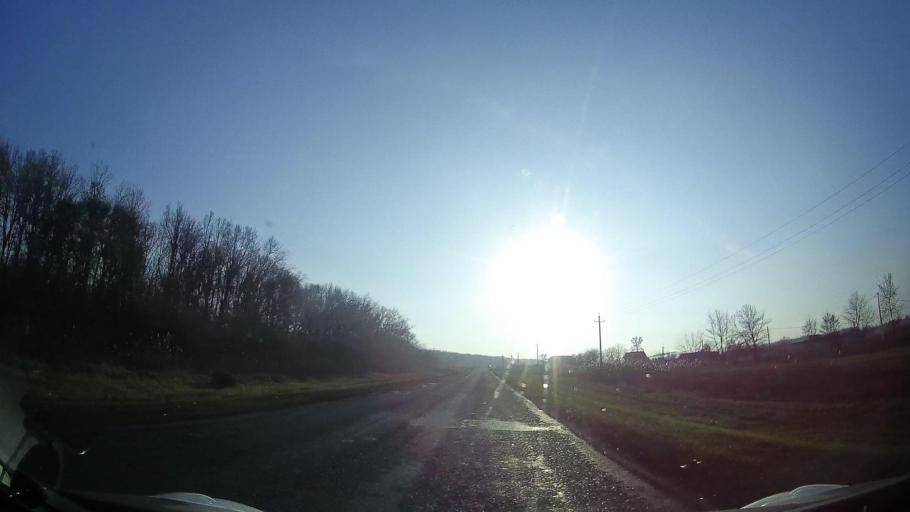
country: RU
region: Rostov
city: Ol'ginskaya
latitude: 47.1394
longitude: 39.8980
